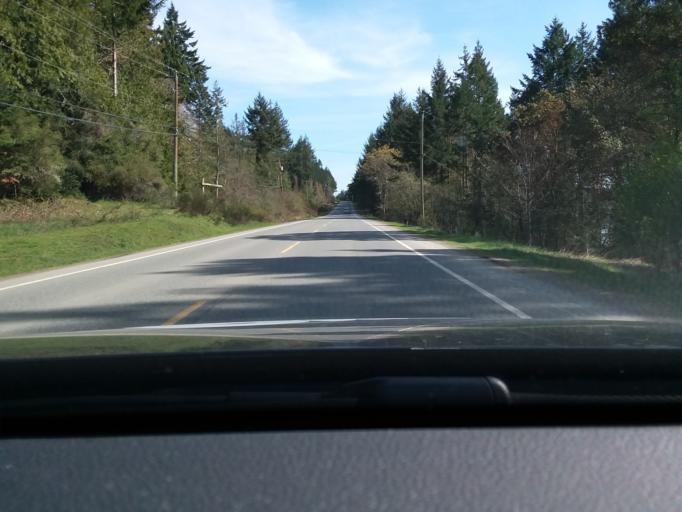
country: CA
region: British Columbia
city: North Cowichan
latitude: 48.8616
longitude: -123.4901
